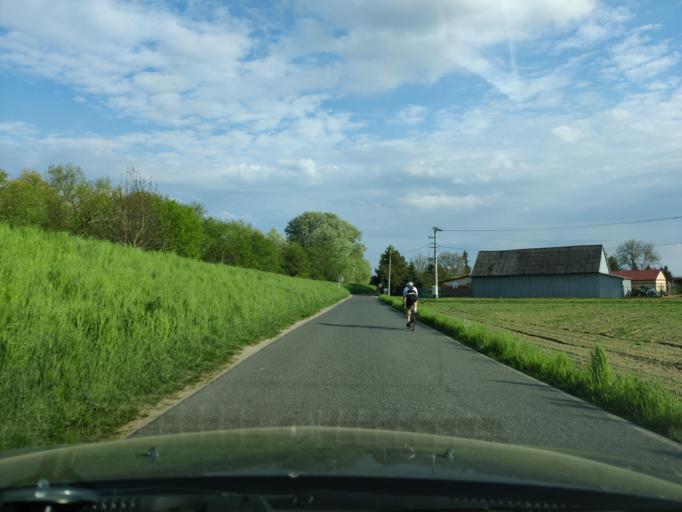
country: PL
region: Masovian Voivodeship
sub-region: Powiat otwocki
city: Jozefow
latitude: 52.1160
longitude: 21.1814
